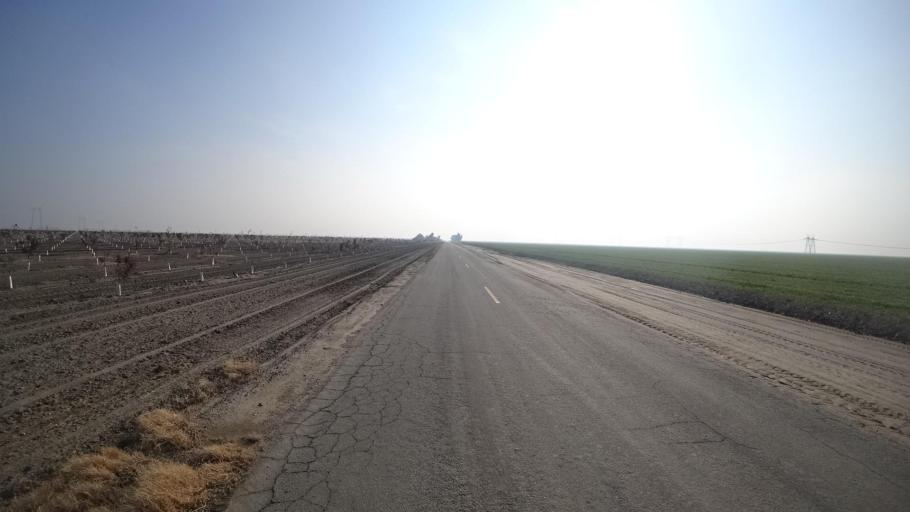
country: US
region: California
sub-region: Kern County
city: Greenfield
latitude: 35.1674
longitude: -119.0393
